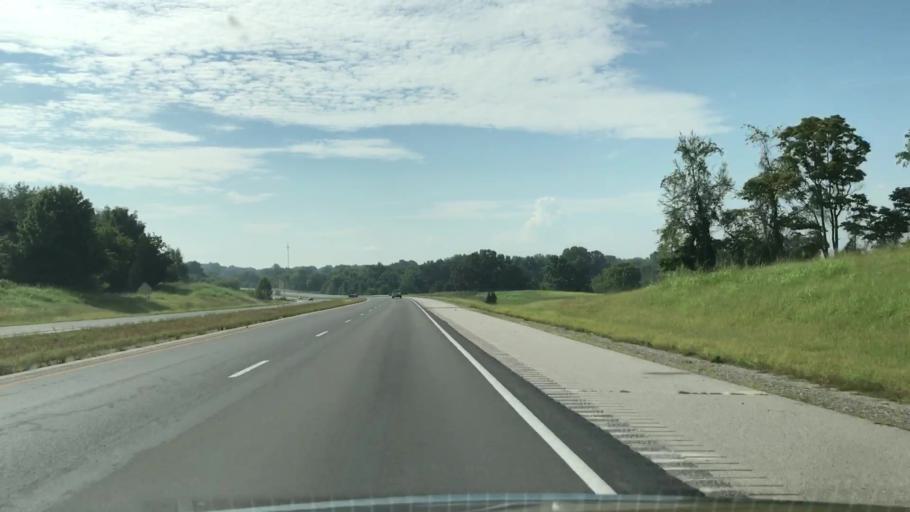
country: US
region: Kentucky
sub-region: Warren County
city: Plano
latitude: 36.8708
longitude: -86.3540
